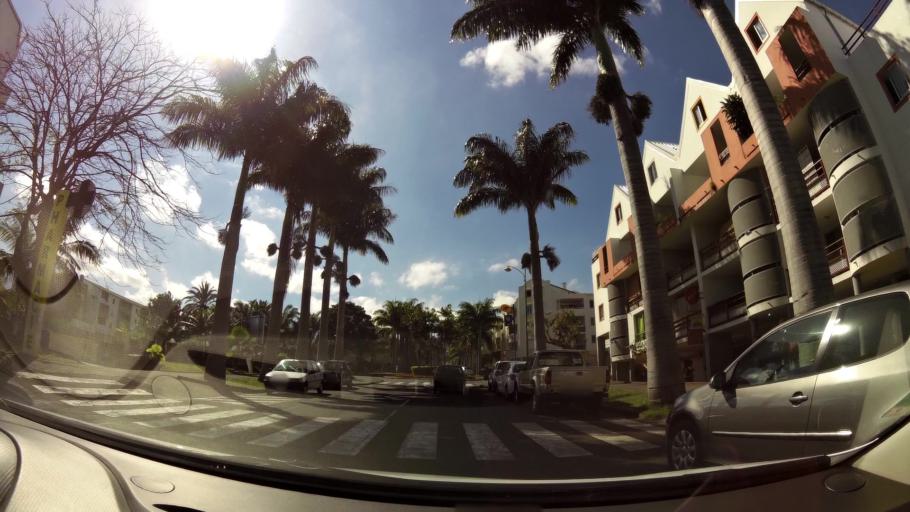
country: RE
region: Reunion
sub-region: Reunion
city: Le Tampon
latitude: -21.2773
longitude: 55.5031
